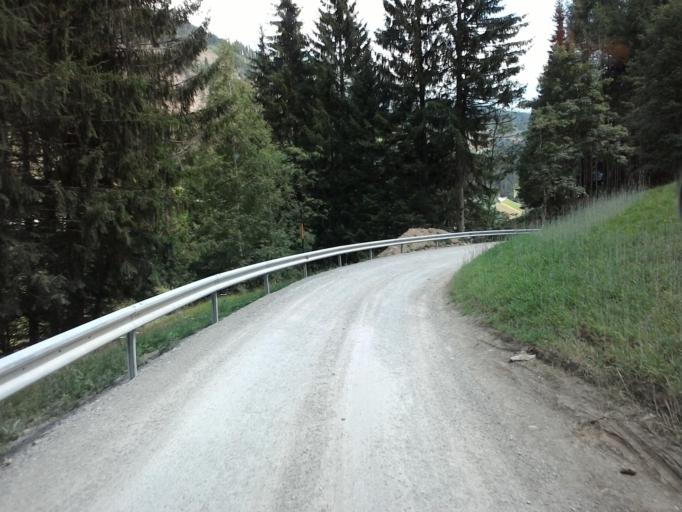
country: AT
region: Tyrol
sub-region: Politischer Bezirk Lienz
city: Untertilliach
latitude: 46.6990
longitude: 12.7523
